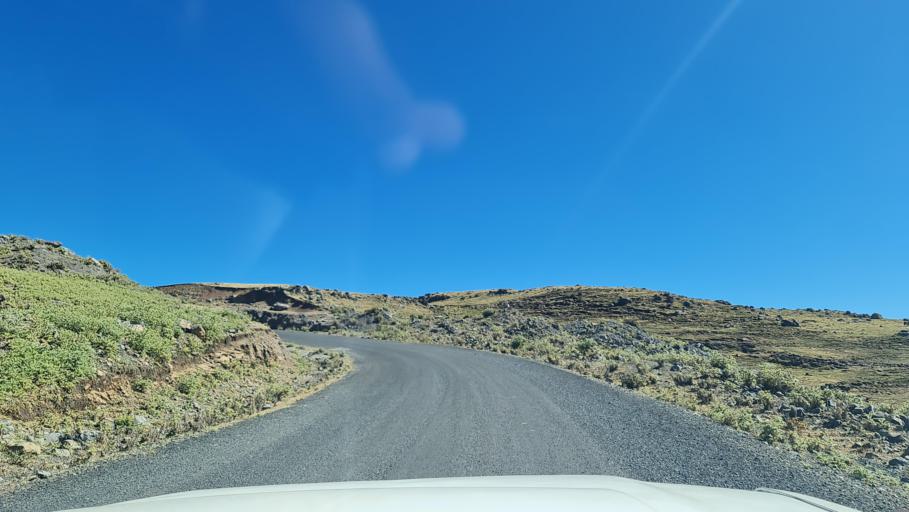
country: ET
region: Amhara
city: Debark'
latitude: 13.1359
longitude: 38.1776
